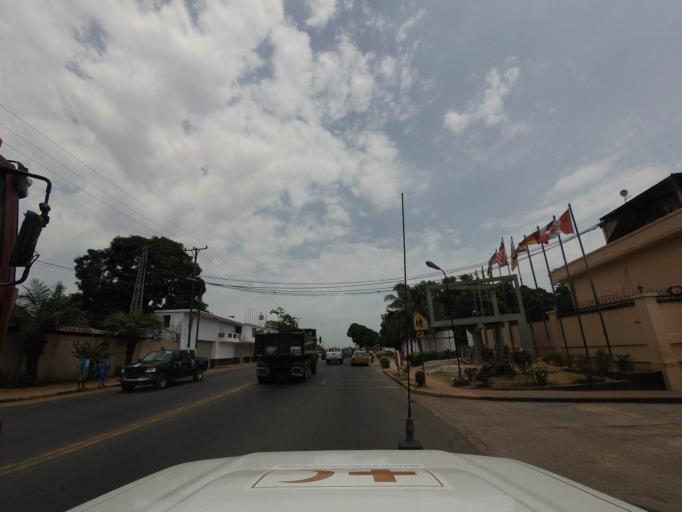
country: LR
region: Montserrado
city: Monrovia
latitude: 6.2661
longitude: -10.7207
